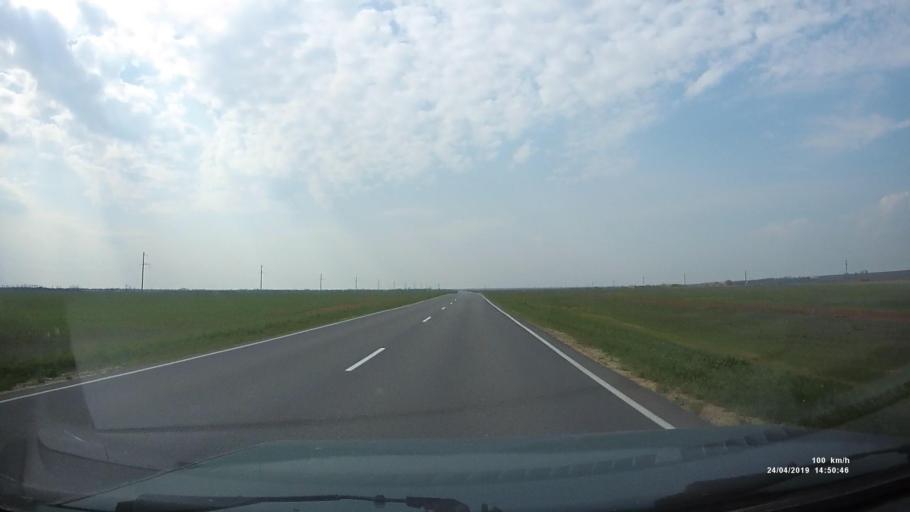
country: RU
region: Rostov
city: Remontnoye
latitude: 46.5198
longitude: 43.7134
